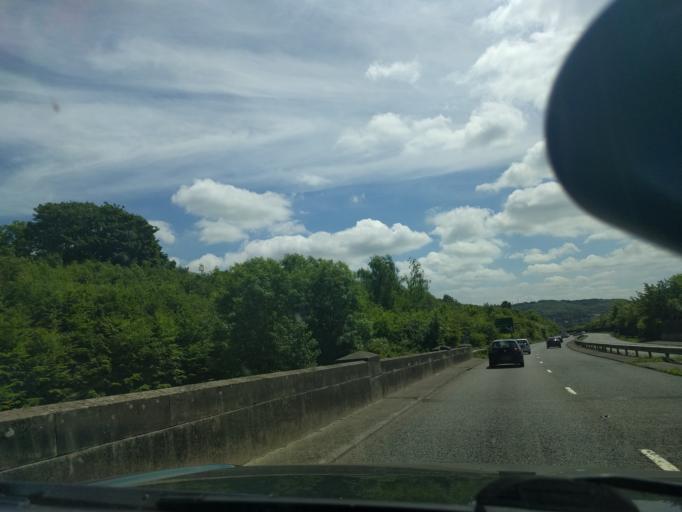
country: GB
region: England
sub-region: Bath and North East Somerset
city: Bath
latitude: 51.4120
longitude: -2.3438
